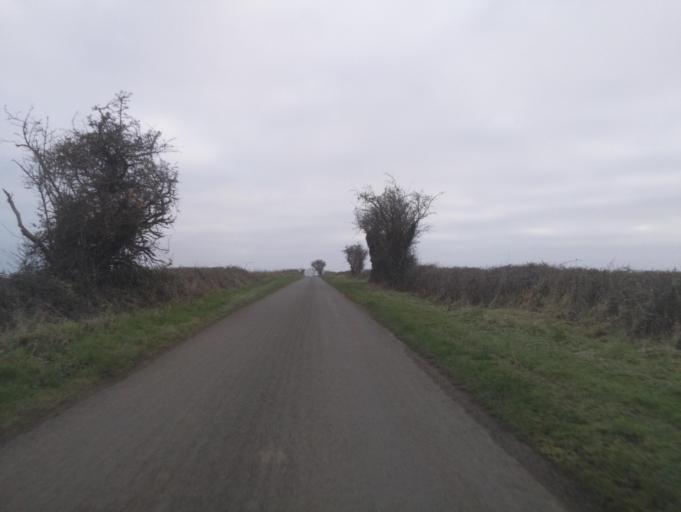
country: GB
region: England
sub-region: Wiltshire
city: Nettleton
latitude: 51.4835
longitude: -2.2834
